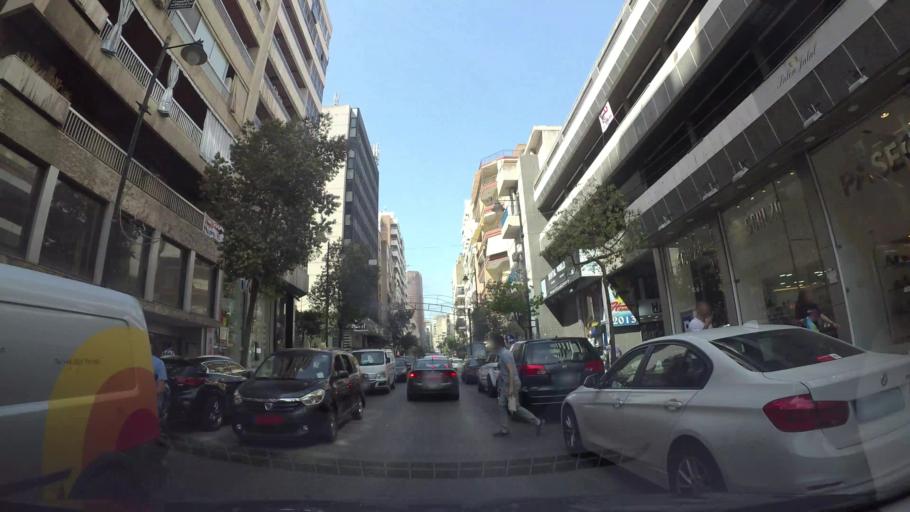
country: LB
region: Beyrouth
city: Beirut
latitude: 33.8832
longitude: 35.4916
